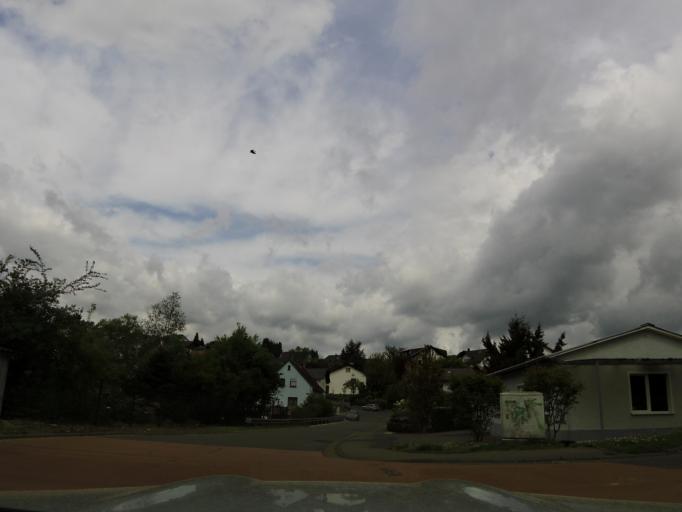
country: DE
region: Hesse
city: Oberbiel
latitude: 50.5555
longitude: 8.4366
